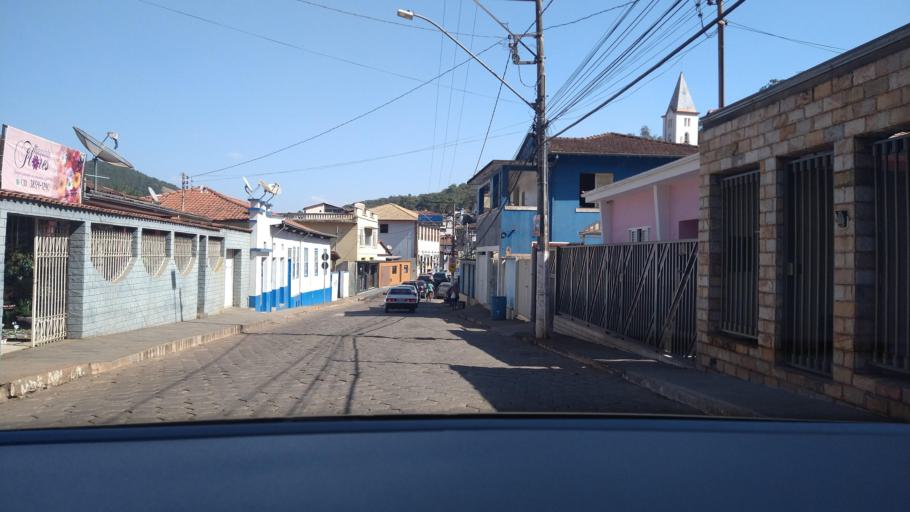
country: BR
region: Minas Gerais
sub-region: Rio Piracicaba
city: Rio Piracicaba
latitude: -19.9285
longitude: -43.1728
